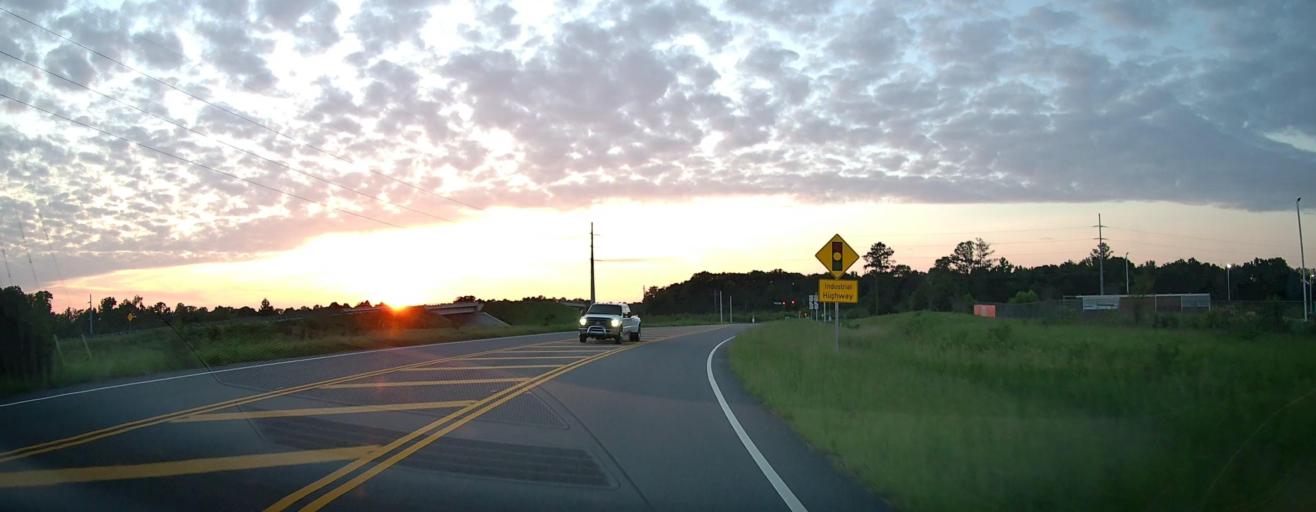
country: US
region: Georgia
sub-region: Houston County
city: Centerville
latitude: 32.6890
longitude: -83.6802
